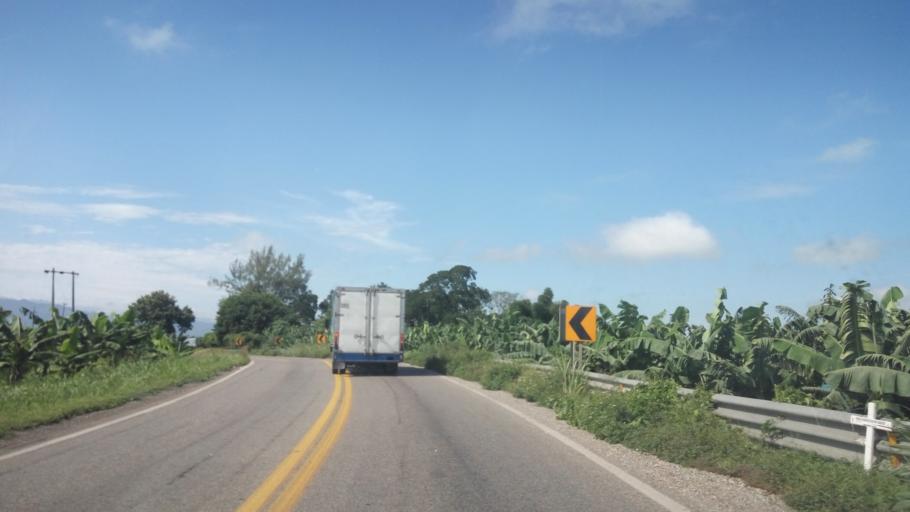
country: MX
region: Tabasco
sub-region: Teapa
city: Eureka y Belen
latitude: 17.6520
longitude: -92.9636
